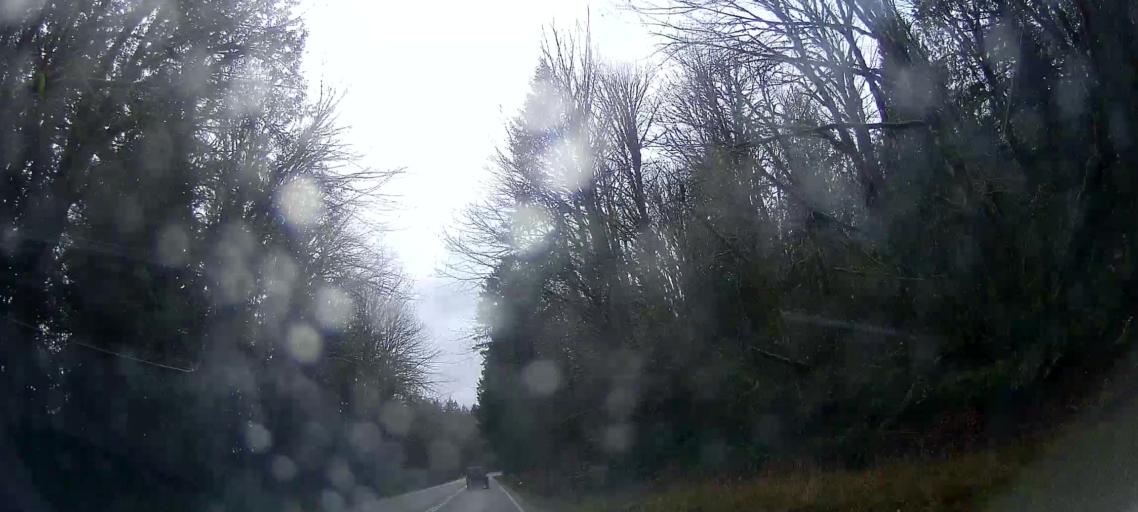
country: US
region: Washington
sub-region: Snohomish County
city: Darrington
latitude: 48.4920
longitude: -121.5518
